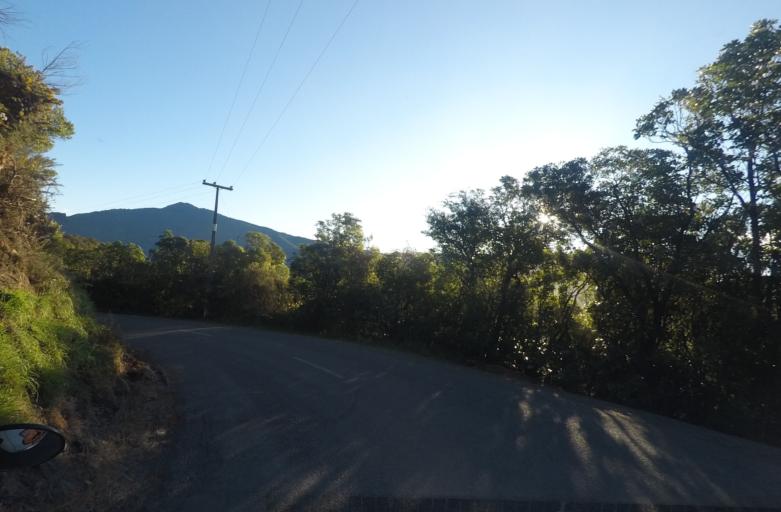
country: NZ
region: Marlborough
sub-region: Marlborough District
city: Picton
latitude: -41.2685
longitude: 173.9456
